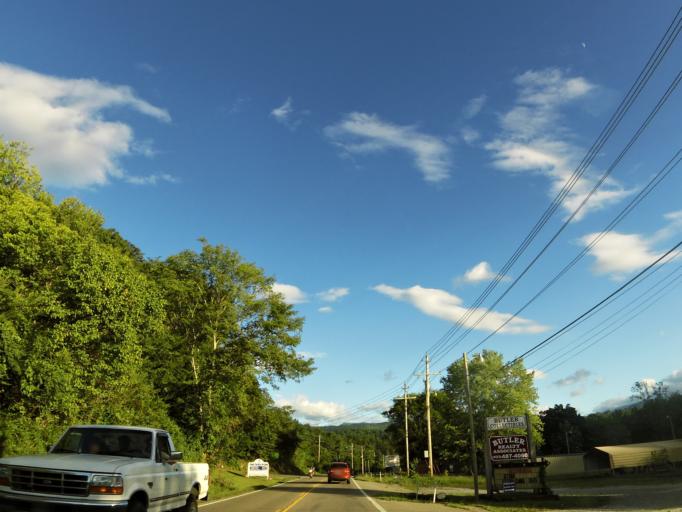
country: US
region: Tennessee
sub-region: Cocke County
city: Newport
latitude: 35.8597
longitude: -83.2201
